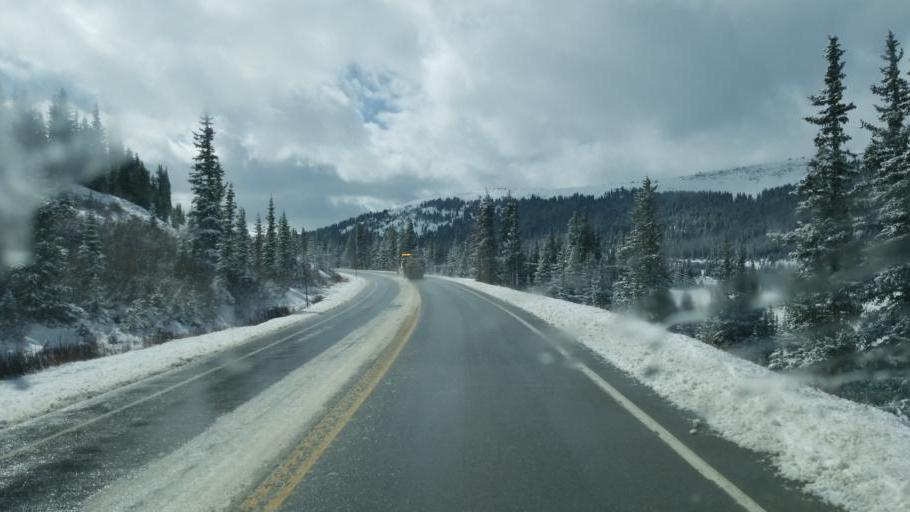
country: US
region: Colorado
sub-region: Lake County
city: Leadville
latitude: 39.3893
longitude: -106.1911
